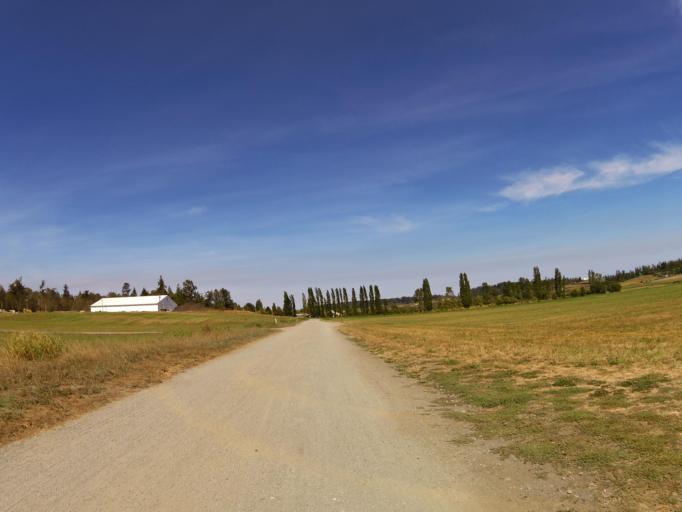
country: CA
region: British Columbia
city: North Saanich
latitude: 48.5544
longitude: -123.3862
